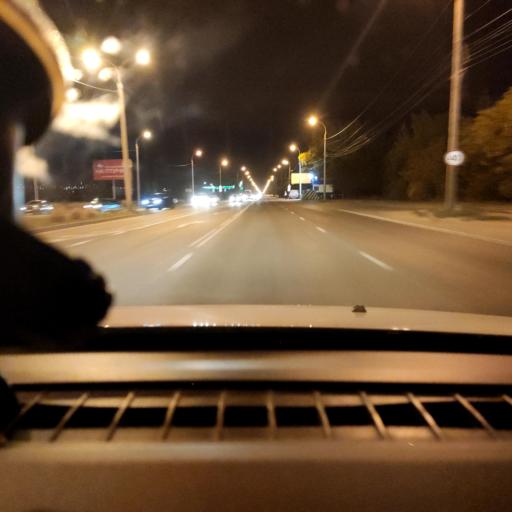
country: RU
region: Samara
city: Samara
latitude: 53.1427
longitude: 50.1805
